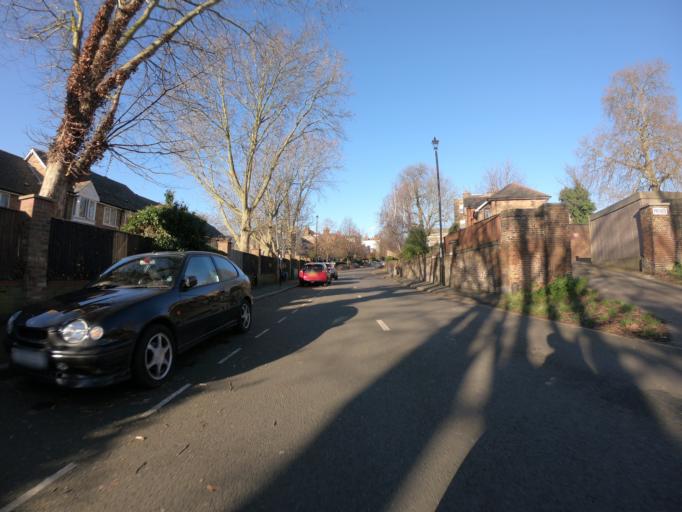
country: GB
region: England
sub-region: Greater London
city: Blackheath
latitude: 51.4697
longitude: -0.0087
